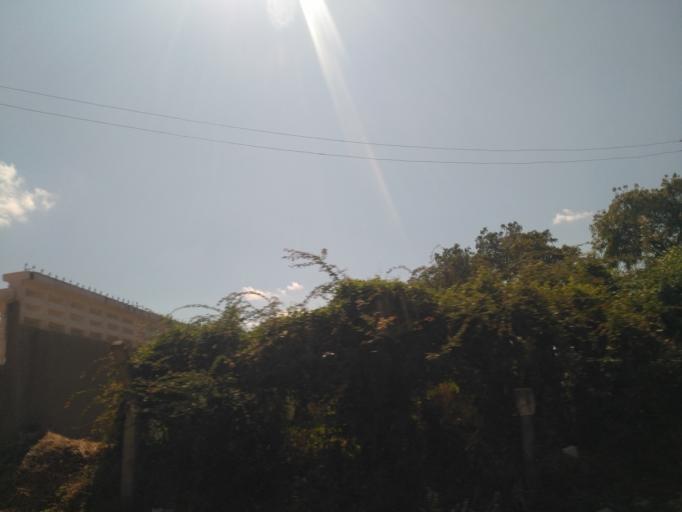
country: TZ
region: Dodoma
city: Dodoma
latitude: -6.1590
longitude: 35.7565
